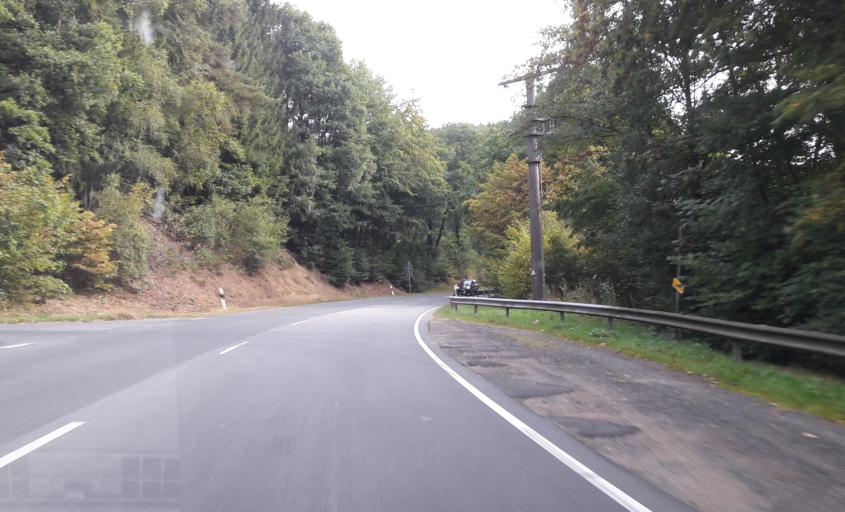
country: DE
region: Saarland
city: Nohfelden
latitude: 49.6020
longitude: 7.1448
